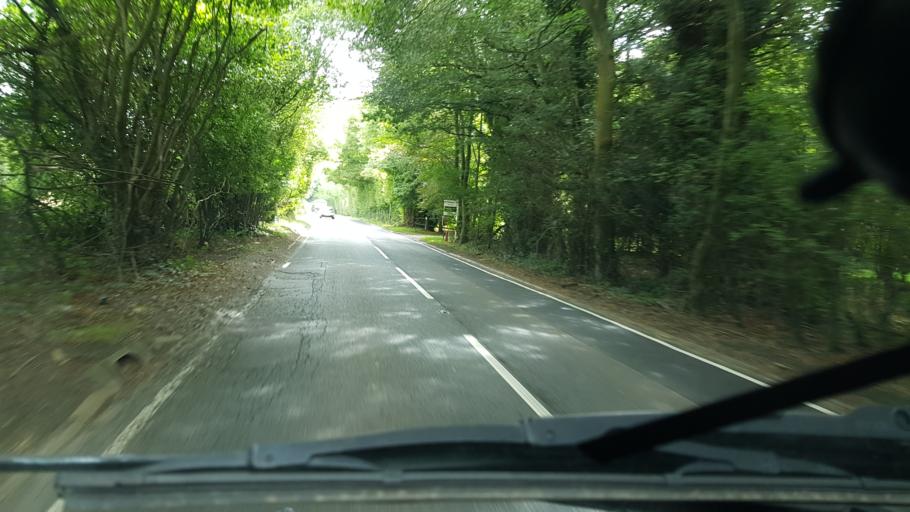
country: GB
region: England
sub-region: Surrey
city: Cranleigh
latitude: 51.1007
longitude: -0.5038
